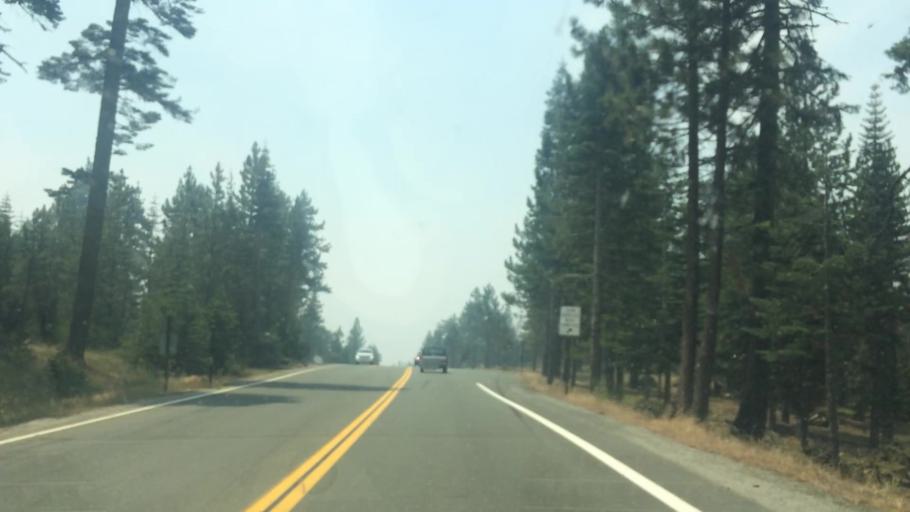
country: US
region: California
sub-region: Amador County
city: Pioneer
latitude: 38.5486
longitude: -120.3053
